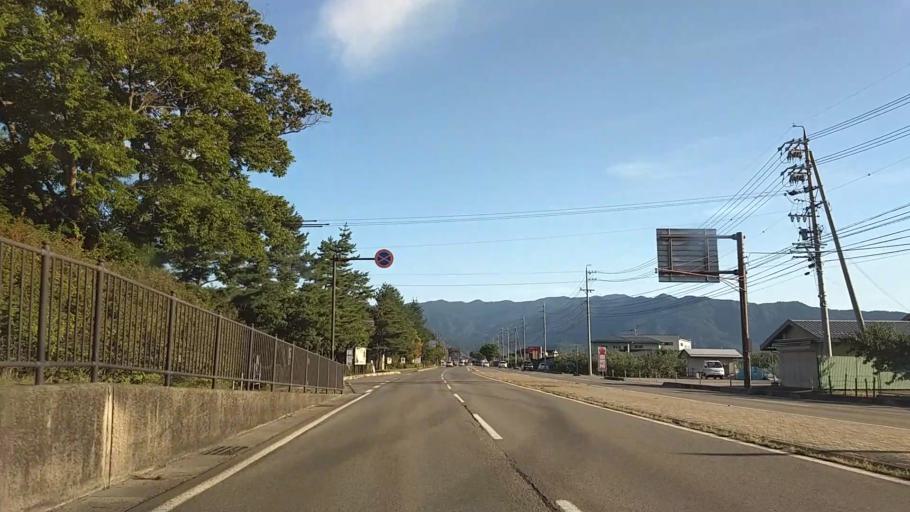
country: JP
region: Nagano
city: Nagano-shi
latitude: 36.5910
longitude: 138.1861
